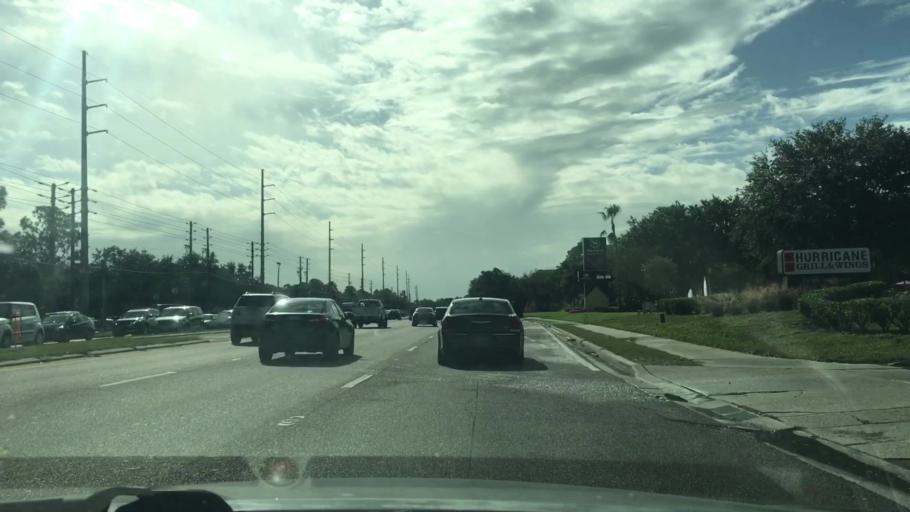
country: US
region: Florida
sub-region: Osceola County
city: Celebration
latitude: 28.3699
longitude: -81.5033
